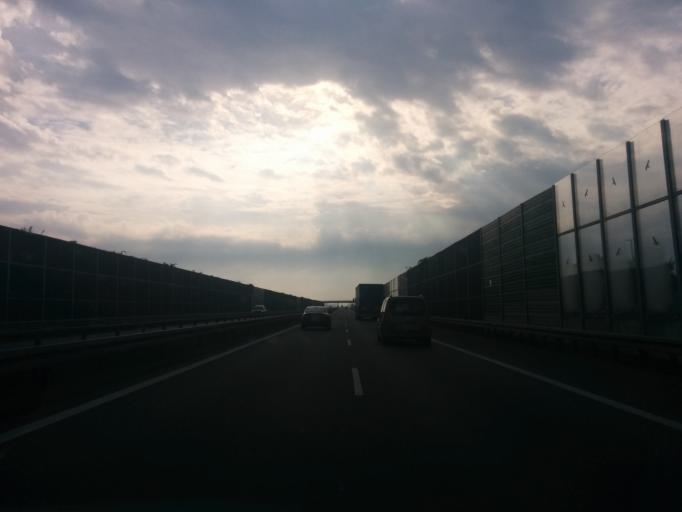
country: PL
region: Masovian Voivodeship
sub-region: Powiat bialobrzeski
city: Stara Blotnica
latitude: 51.5478
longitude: 21.0490
